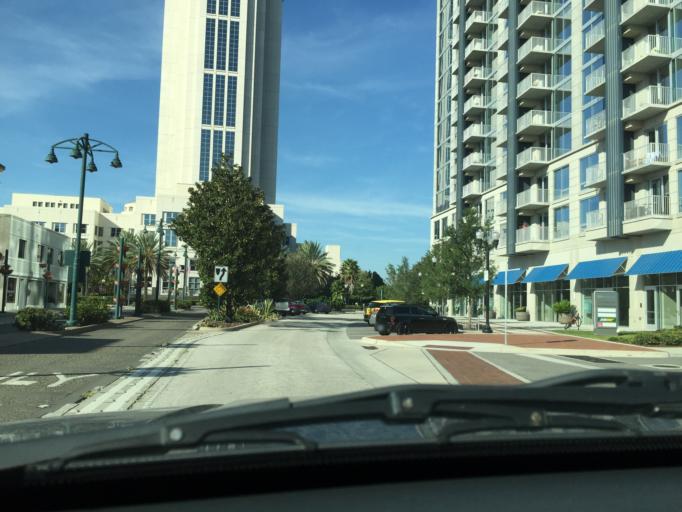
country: US
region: Florida
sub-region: Orange County
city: Orlando
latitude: 28.5465
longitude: -81.3775
